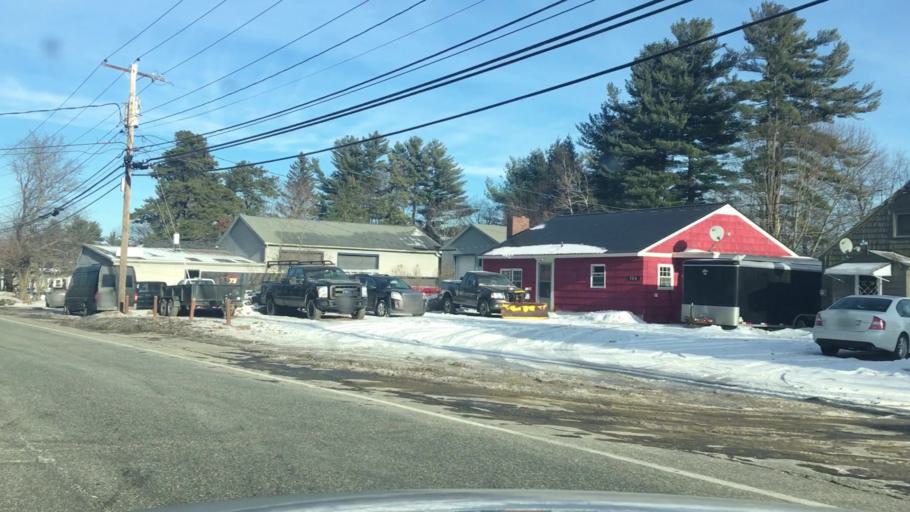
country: US
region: Maine
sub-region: Androscoggin County
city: Auburn
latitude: 44.0665
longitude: -70.2477
